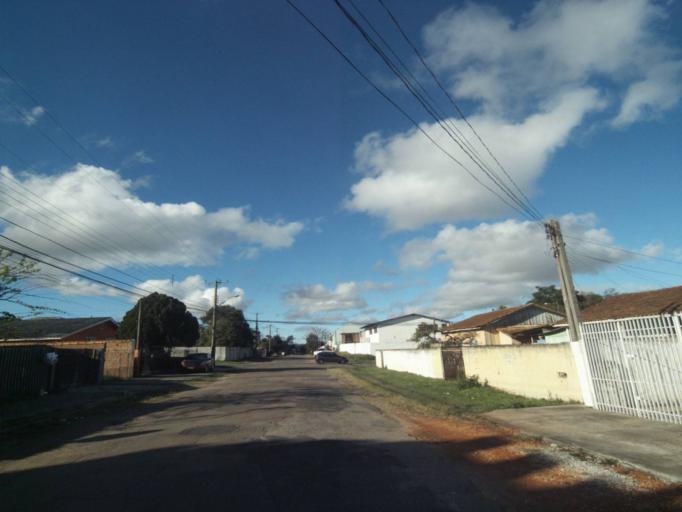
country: BR
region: Parana
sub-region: Sao Jose Dos Pinhais
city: Sao Jose dos Pinhais
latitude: -25.5256
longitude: -49.2910
